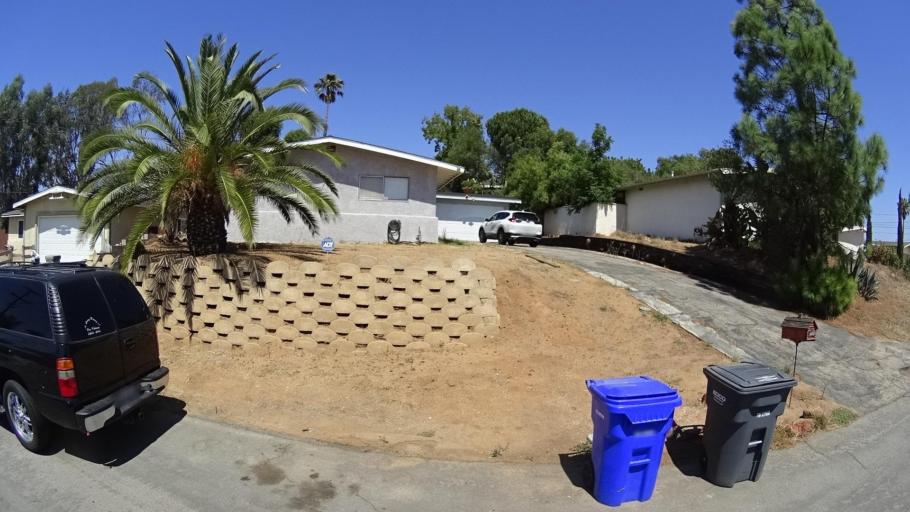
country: US
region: California
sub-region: San Diego County
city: Fallbrook
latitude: 33.3794
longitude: -117.2589
